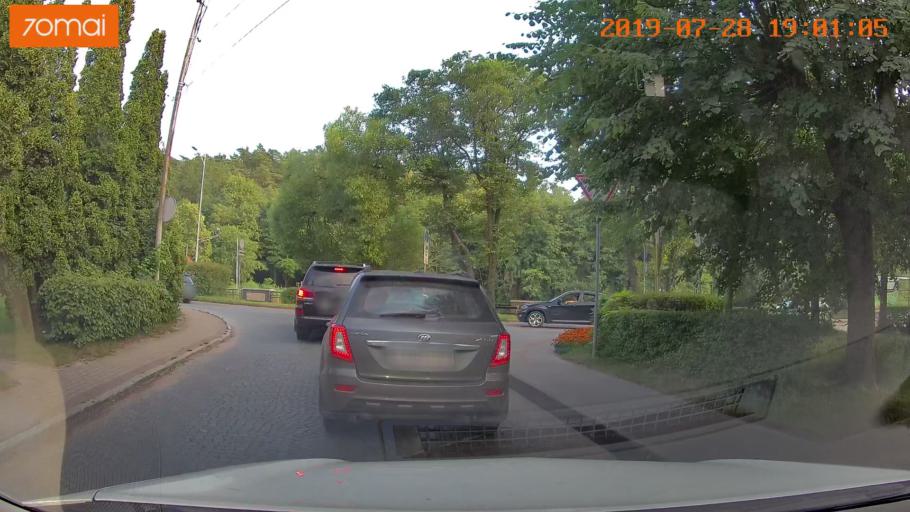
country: RU
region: Kaliningrad
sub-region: Gorod Svetlogorsk
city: Svetlogorsk
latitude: 54.9385
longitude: 20.1582
